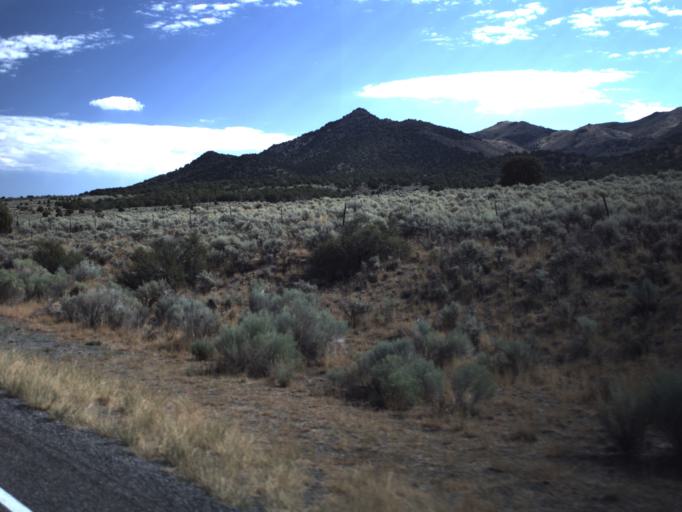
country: US
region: Utah
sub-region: Juab County
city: Mona
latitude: 39.8299
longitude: -112.1394
